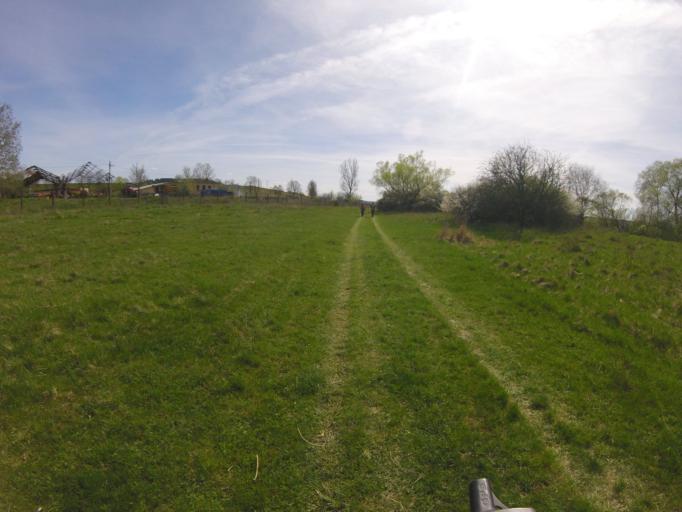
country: HU
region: Borsod-Abauj-Zemplen
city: Szendro
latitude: 48.4193
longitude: 20.7287
